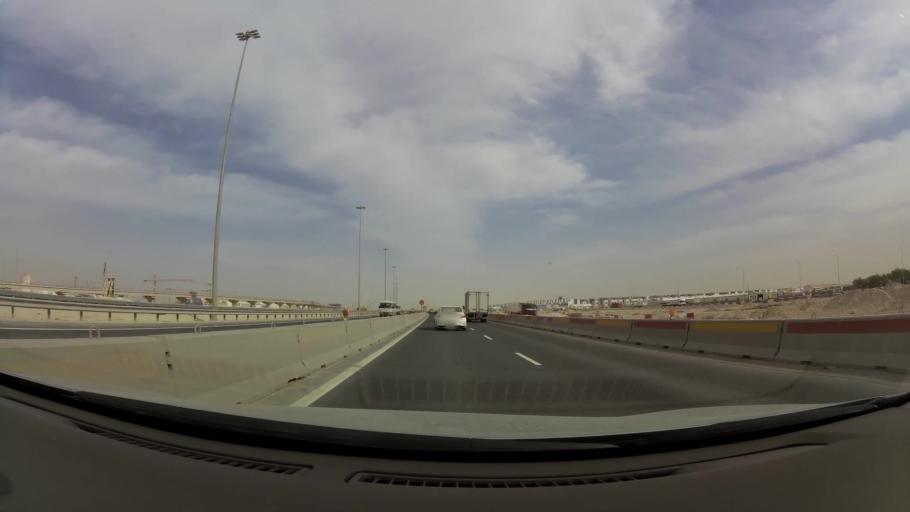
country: QA
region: Baladiyat ar Rayyan
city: Ar Rayyan
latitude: 25.3290
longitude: 51.3354
